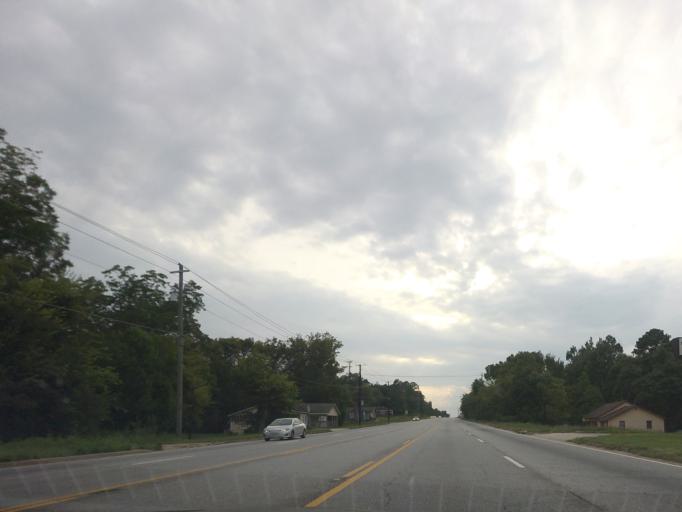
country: US
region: Georgia
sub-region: Bibb County
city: Macon
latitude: 32.8417
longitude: -83.5588
